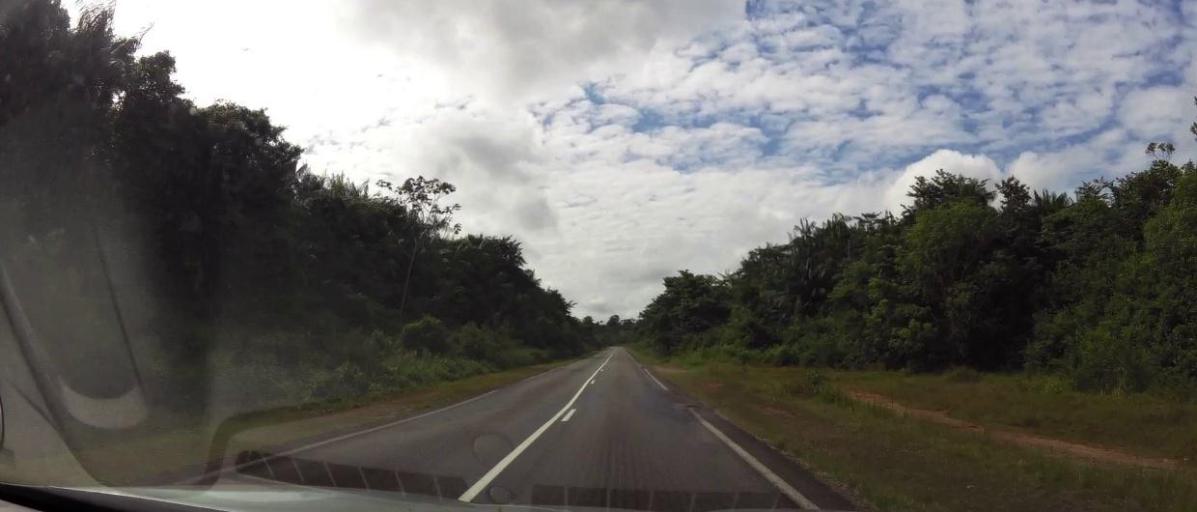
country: GF
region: Guyane
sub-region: Guyane
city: Sinnamary
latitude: 5.3722
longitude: -52.9656
